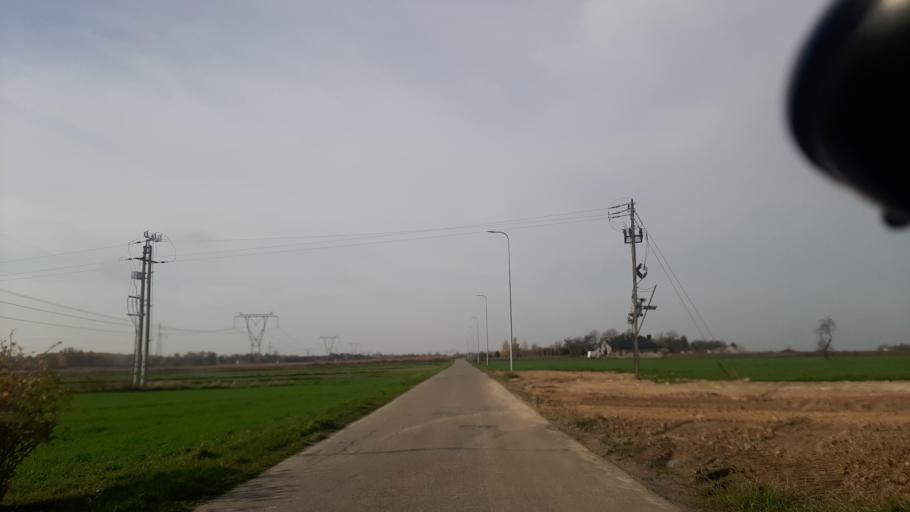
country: PL
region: Lublin Voivodeship
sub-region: Powiat lubelski
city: Lublin
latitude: 51.3338
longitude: 22.5298
